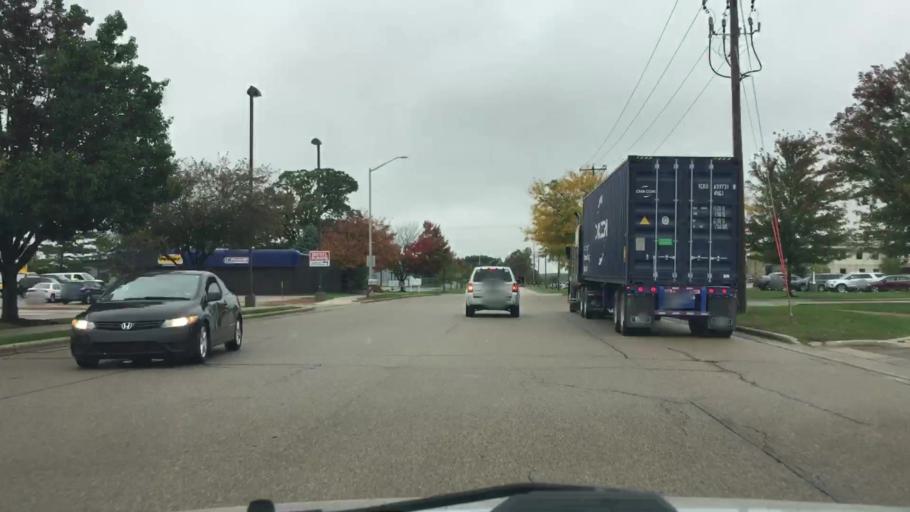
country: US
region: Wisconsin
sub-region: Rock County
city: Janesville
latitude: 42.7300
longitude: -88.9913
